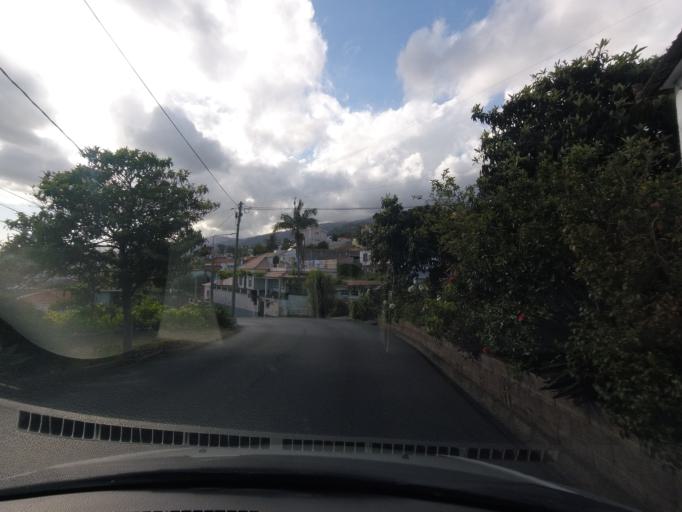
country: PT
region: Madeira
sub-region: Funchal
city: Nossa Senhora do Monte
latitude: 32.6585
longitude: -16.8925
